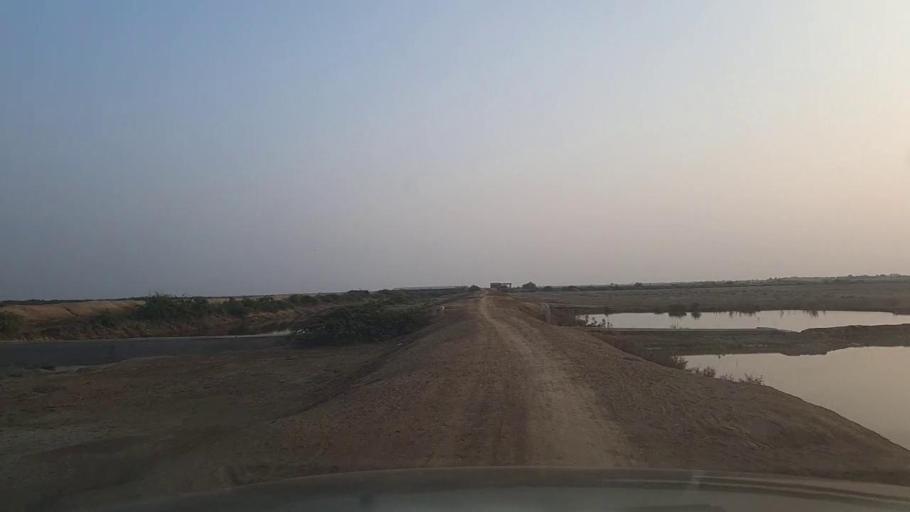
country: PK
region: Sindh
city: Jati
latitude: 24.5330
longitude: 68.4089
